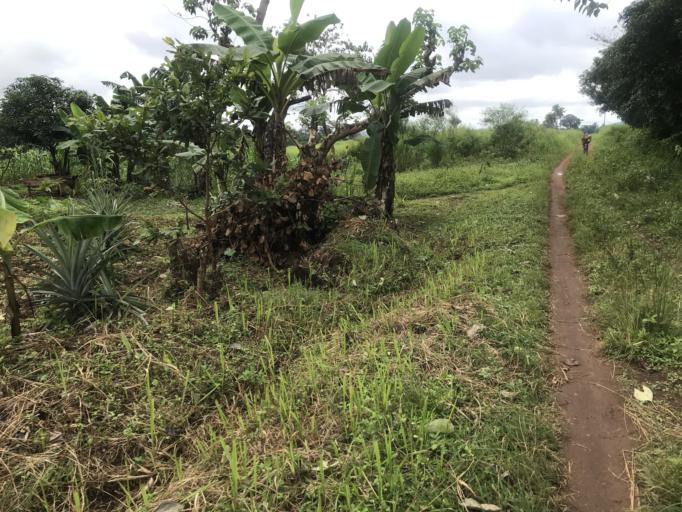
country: SL
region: Eastern Province
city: Buedu
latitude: 8.4644
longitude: -10.3166
